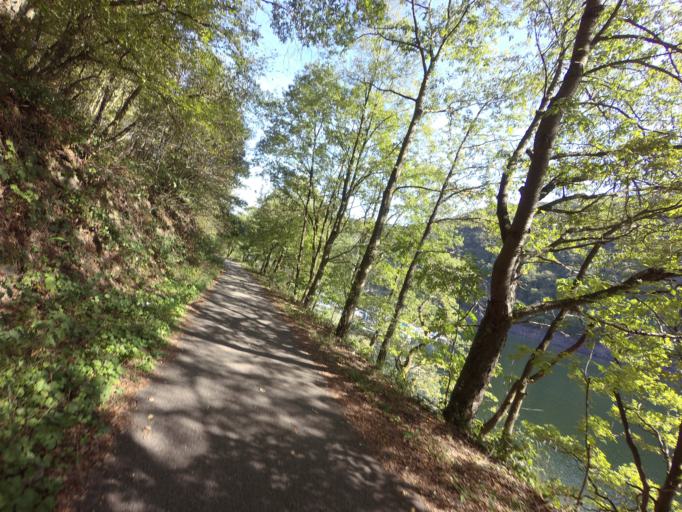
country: DE
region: North Rhine-Westphalia
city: Heimbach
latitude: 50.6150
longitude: 6.3931
